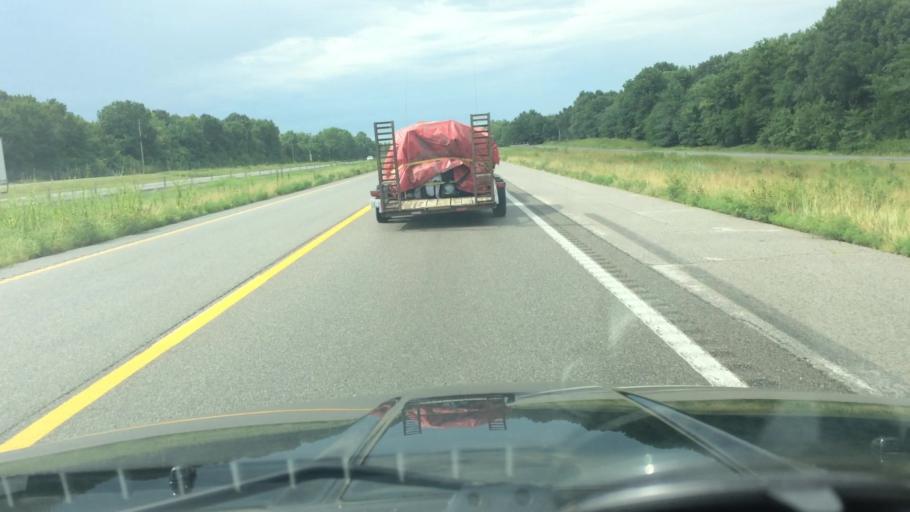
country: US
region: Missouri
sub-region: Cass County
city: Peculiar
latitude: 38.6842
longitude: -94.4231
